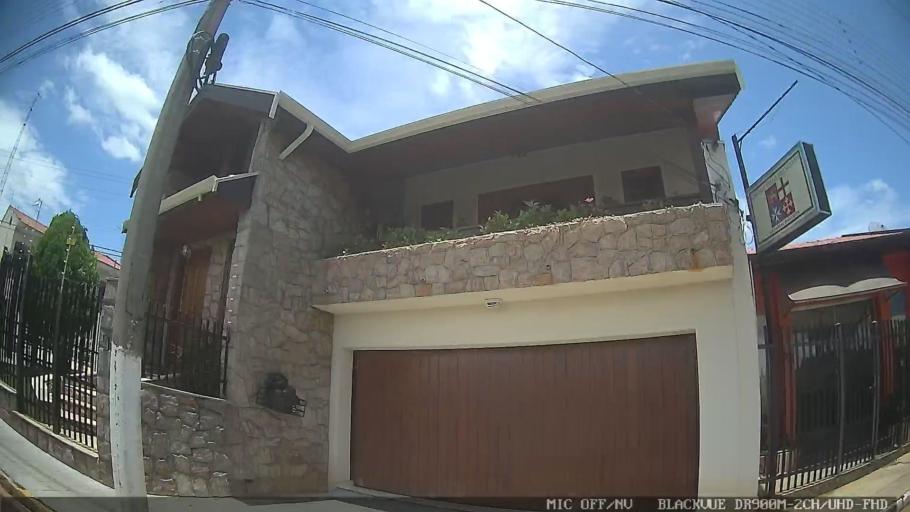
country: BR
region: Sao Paulo
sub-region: Laranjal Paulista
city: Laranjal Paulista
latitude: -23.0526
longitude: -47.8332
